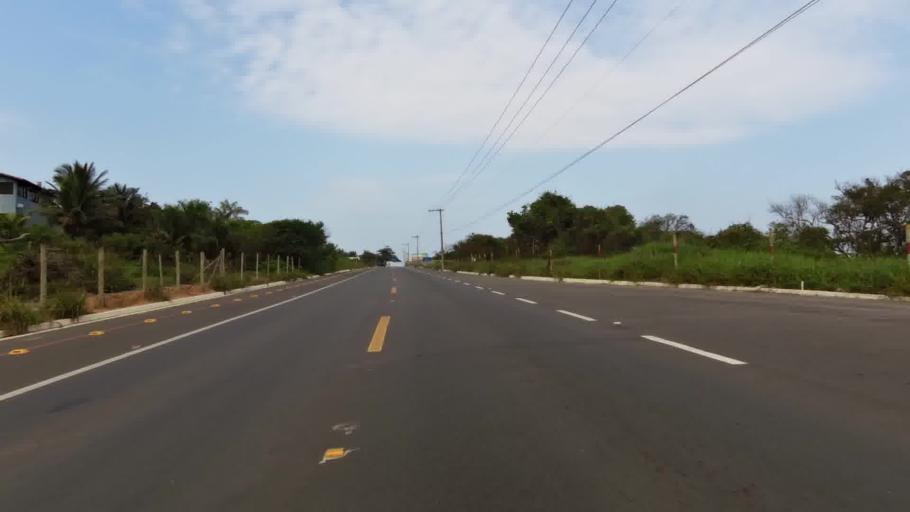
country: BR
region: Espirito Santo
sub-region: Piuma
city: Piuma
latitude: -20.8175
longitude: -40.6157
